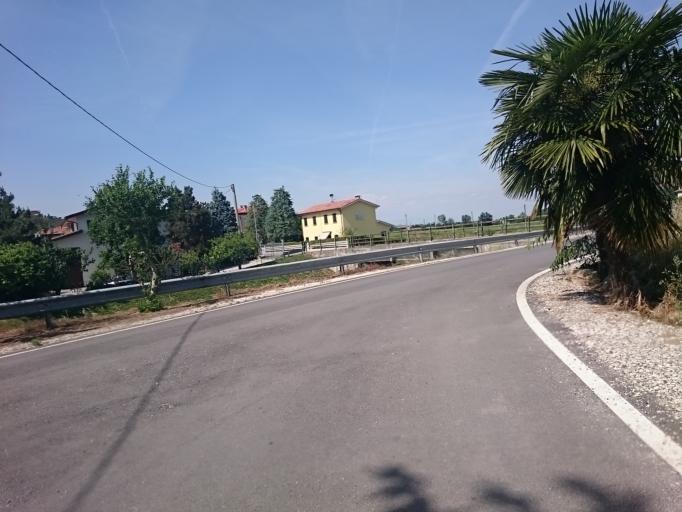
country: IT
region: Veneto
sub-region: Provincia di Padova
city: Vo
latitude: 45.3439
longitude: 11.6238
